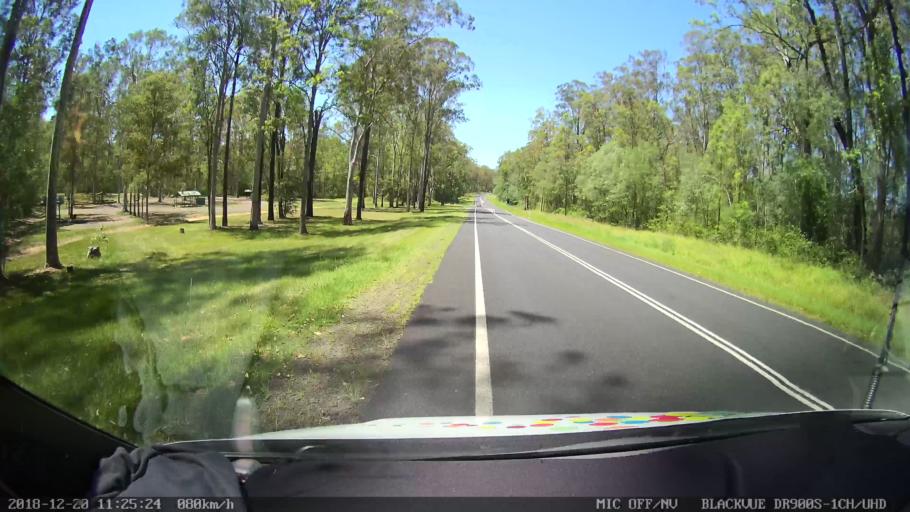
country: AU
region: New South Wales
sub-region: Richmond Valley
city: Casino
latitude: -29.0870
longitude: 153.0010
